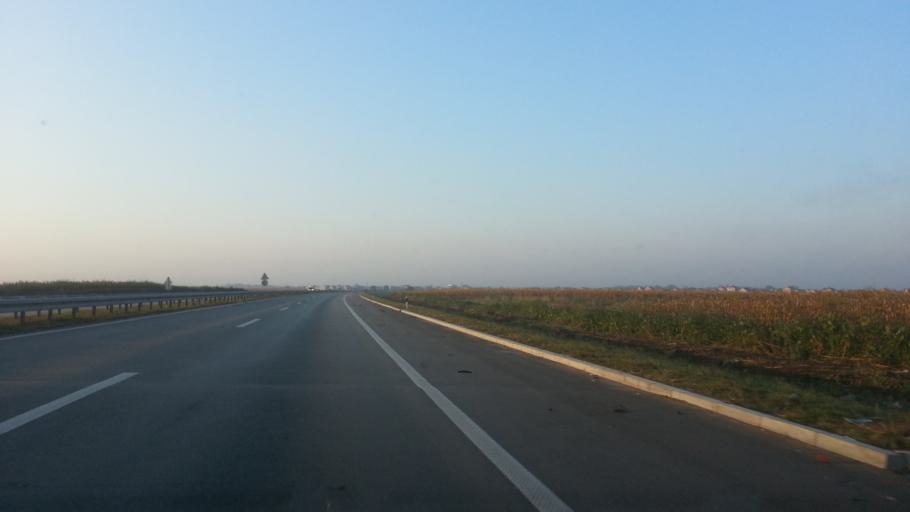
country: RS
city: Novi Banovci
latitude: 44.9131
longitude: 20.3053
